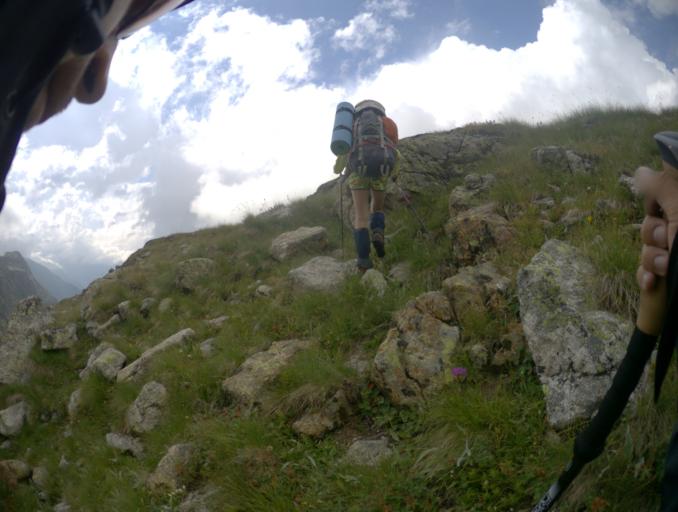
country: RU
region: Karachayevo-Cherkesiya
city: Uchkulan
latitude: 43.2841
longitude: 42.0971
